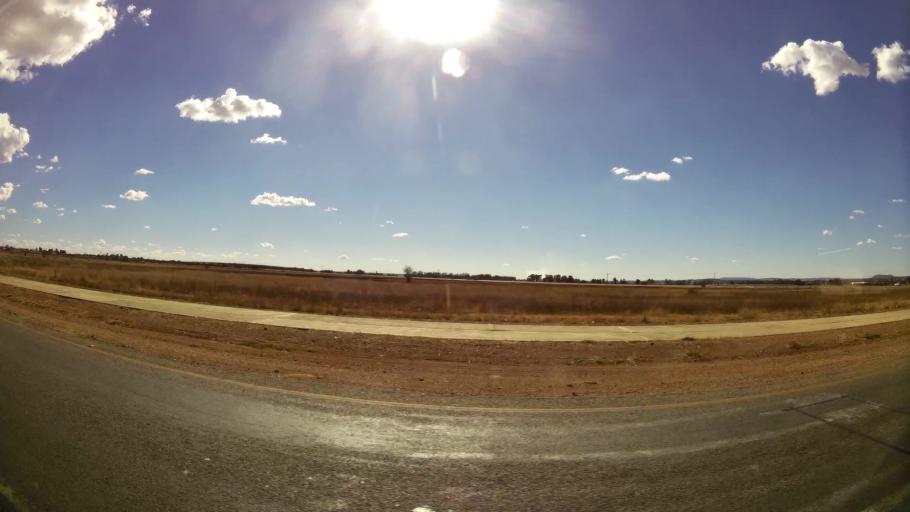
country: ZA
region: North-West
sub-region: Dr Kenneth Kaunda District Municipality
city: Klerksdorp
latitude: -26.8730
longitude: 26.6057
